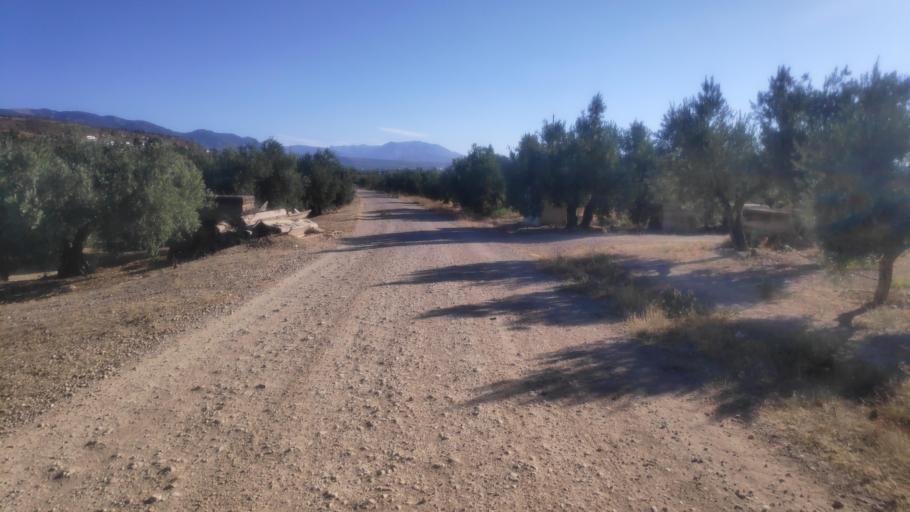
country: ES
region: Andalusia
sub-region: Provincia de Jaen
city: Hinojares
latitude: 37.6579
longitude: -2.9795
